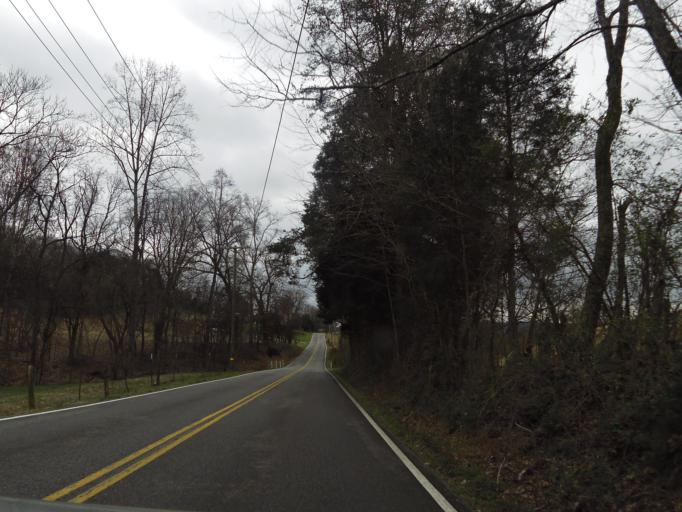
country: US
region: Tennessee
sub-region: Jefferson County
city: Jefferson City
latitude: 36.1889
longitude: -83.5387
